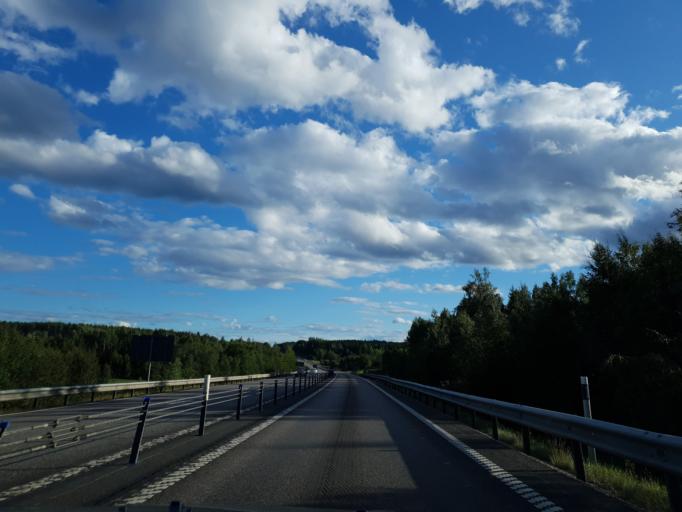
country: SE
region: Vaesternorrland
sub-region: Sundsvalls Kommun
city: Njurundabommen
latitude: 62.2277
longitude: 17.3720
